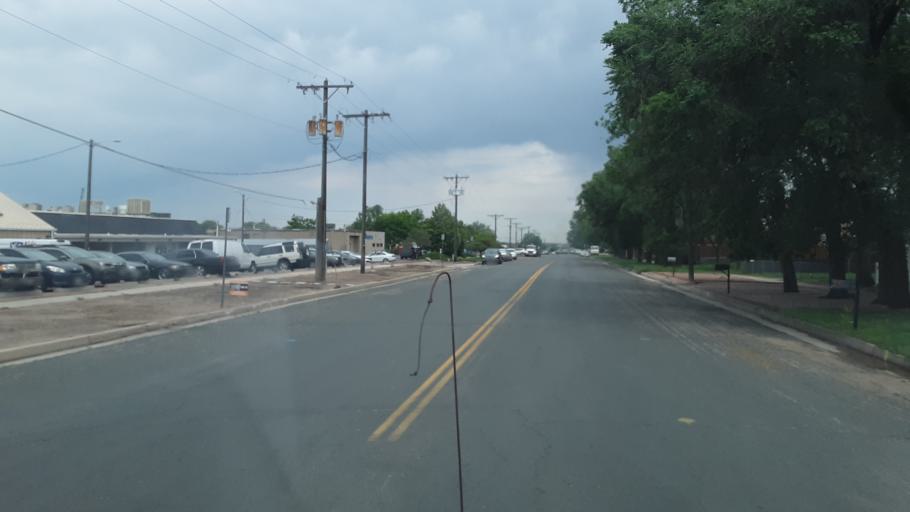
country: US
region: Colorado
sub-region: El Paso County
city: Colorado Springs
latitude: 38.8413
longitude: -104.8639
